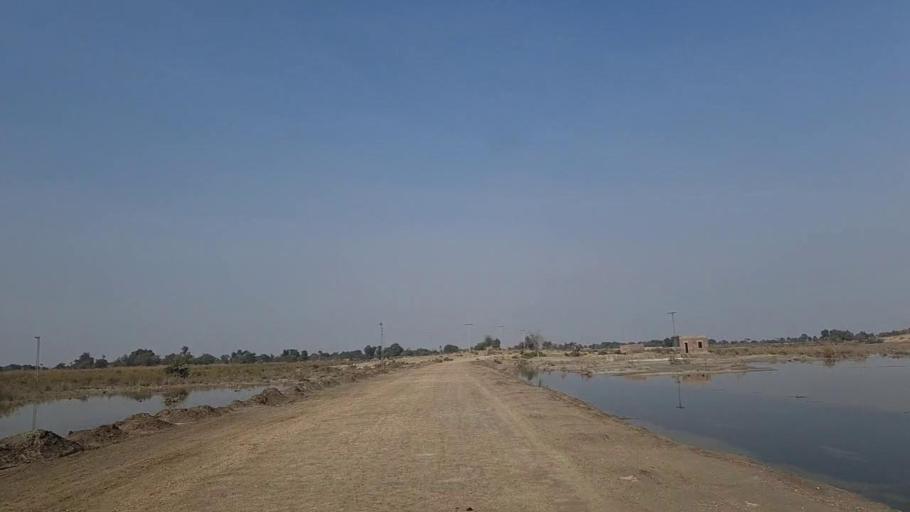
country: PK
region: Sindh
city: Daur
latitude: 26.5087
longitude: 68.4795
